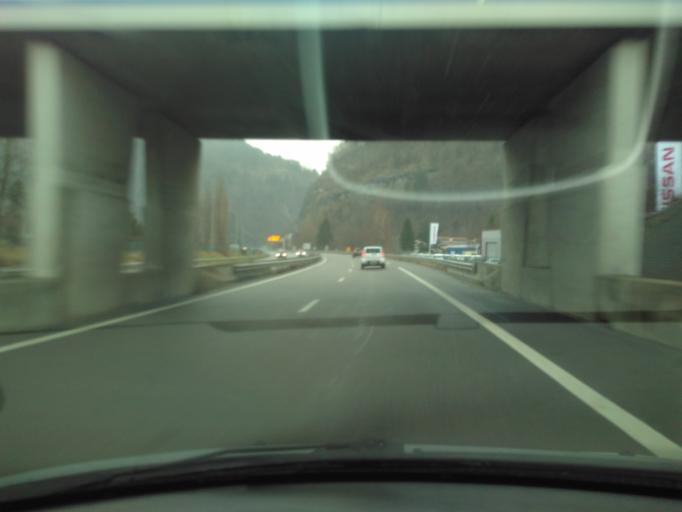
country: FR
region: Rhone-Alpes
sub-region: Departement de la Haute-Savoie
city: Cluses
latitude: 46.0573
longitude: 6.5715
